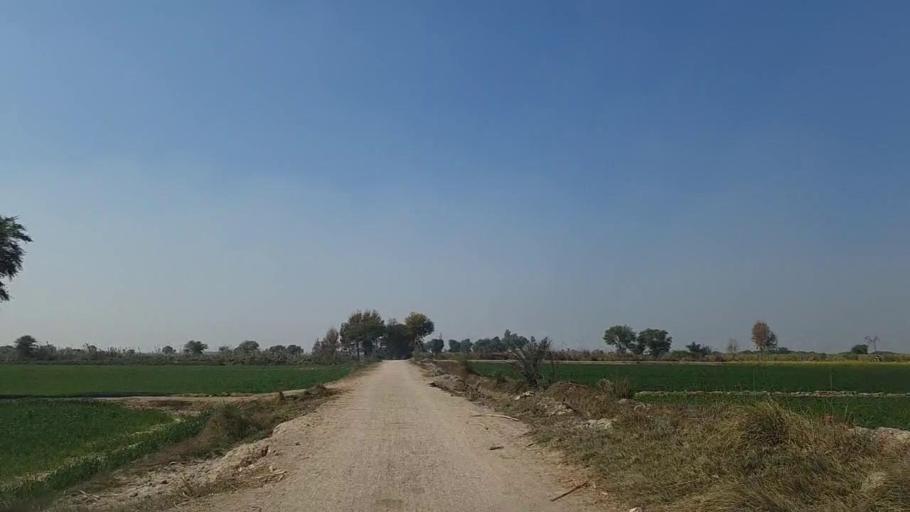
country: PK
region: Sindh
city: Daur
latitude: 26.5002
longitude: 68.3479
